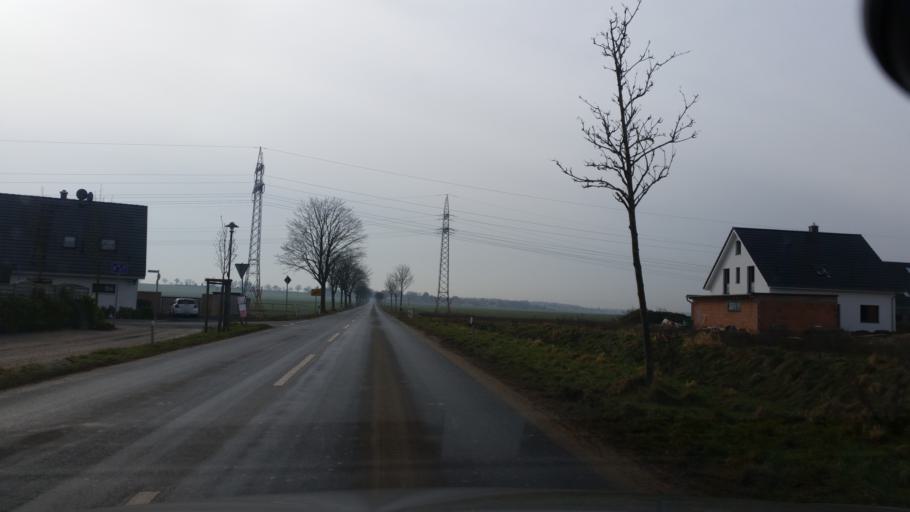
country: DE
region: Lower Saxony
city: Seelze
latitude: 52.3847
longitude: 9.5952
